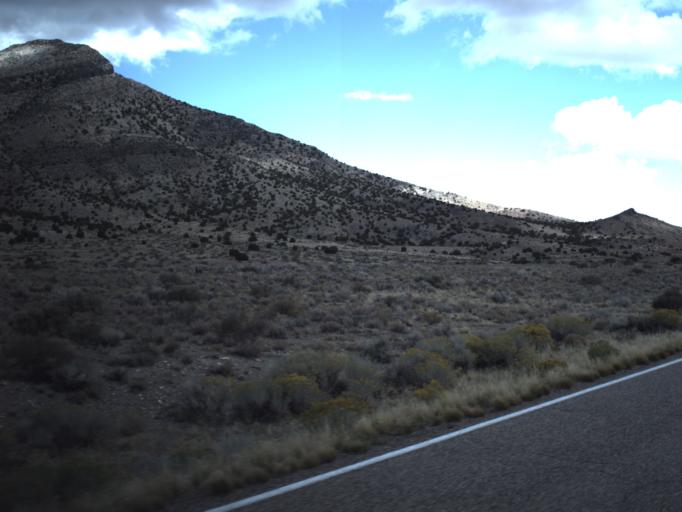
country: US
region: Utah
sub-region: Beaver County
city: Milford
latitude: 38.4354
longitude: -113.2977
